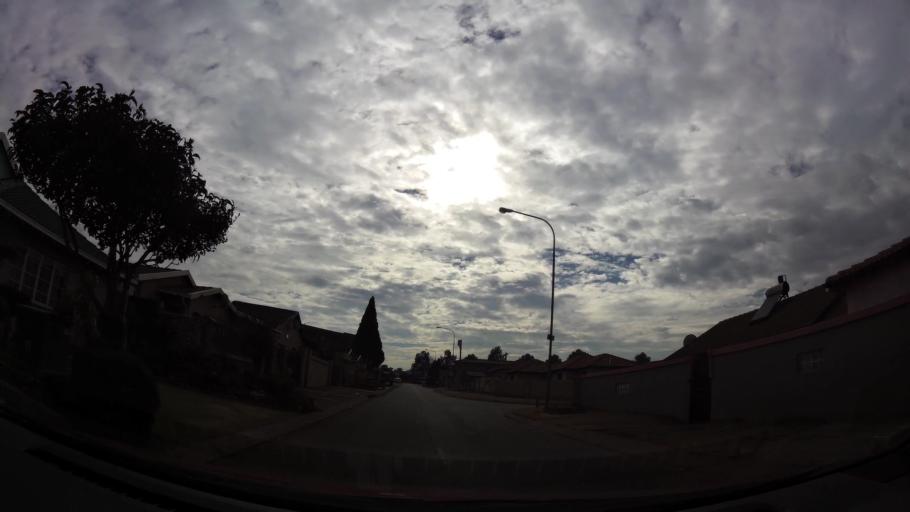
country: ZA
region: Gauteng
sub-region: City of Johannesburg Metropolitan Municipality
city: Soweto
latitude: -26.2779
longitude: 27.8359
